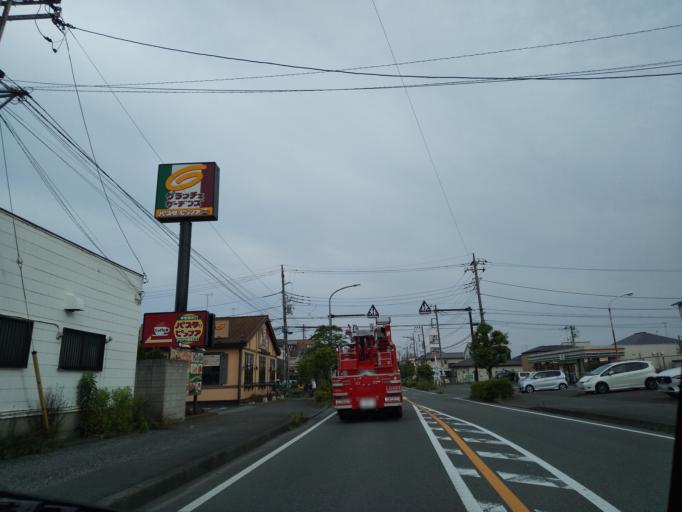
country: JP
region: Kanagawa
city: Atsugi
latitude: 35.4690
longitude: 139.3590
